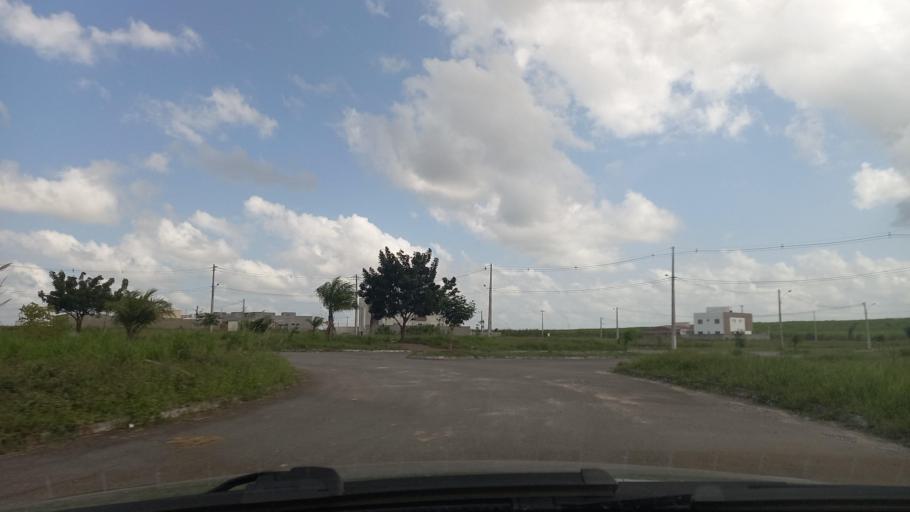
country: BR
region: Pernambuco
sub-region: Goiana
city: Goiana
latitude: -7.5672
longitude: -35.0318
